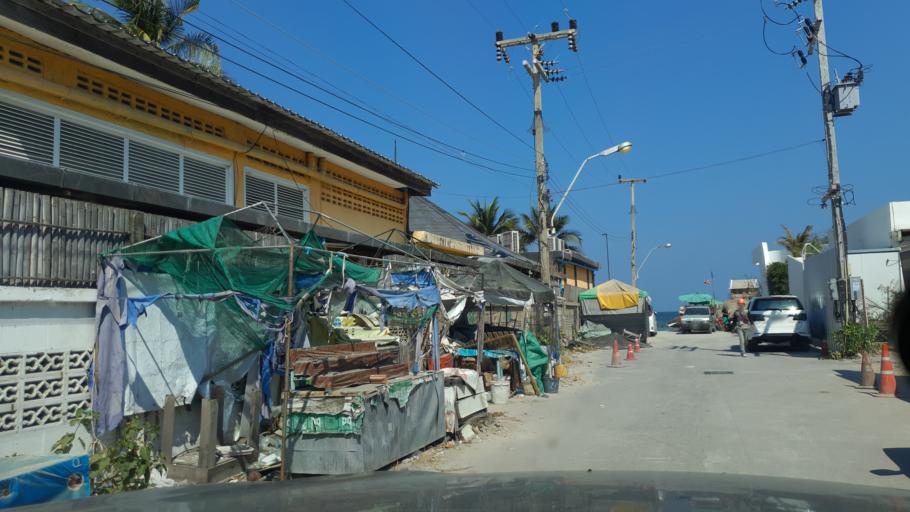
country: TH
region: Prachuap Khiri Khan
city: Hua Hin
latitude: 12.5182
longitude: 99.9777
